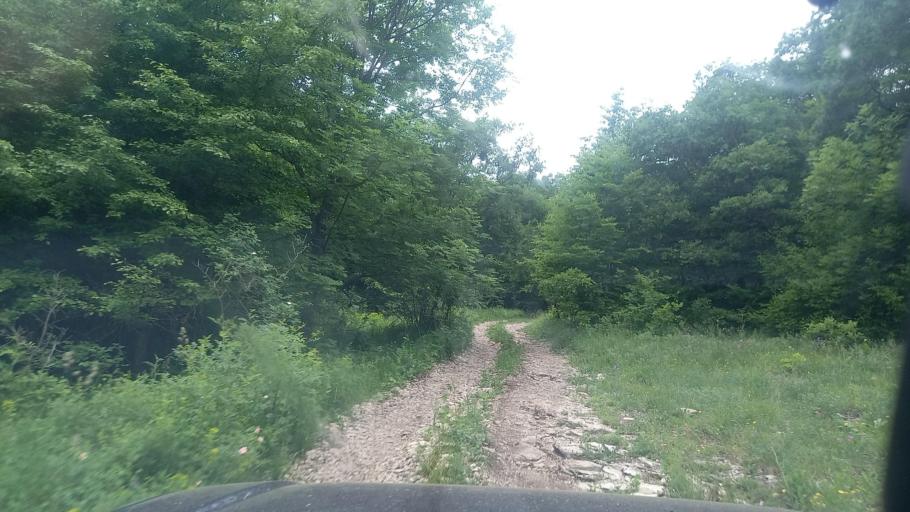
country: RU
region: Karachayevo-Cherkesiya
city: Pregradnaya
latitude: 44.0286
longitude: 41.3041
